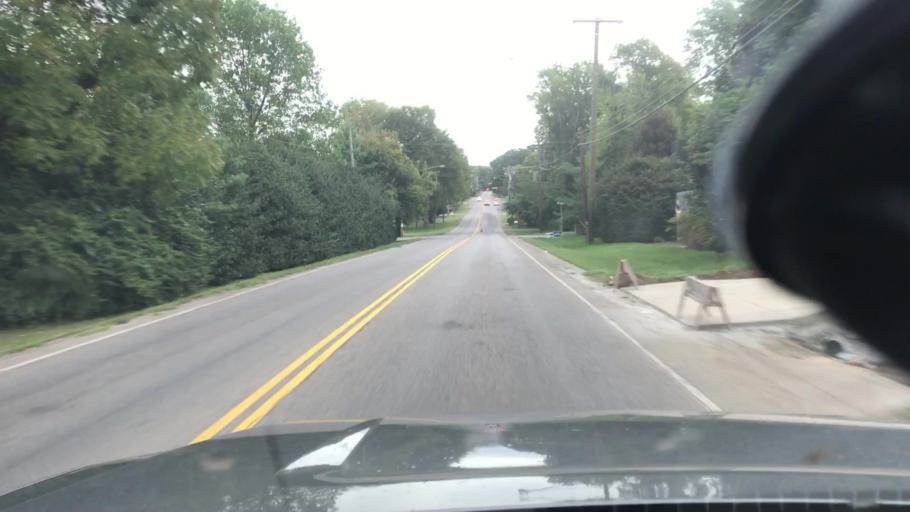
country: US
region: Tennessee
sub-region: Davidson County
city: Oak Hill
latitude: 36.1134
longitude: -86.8041
